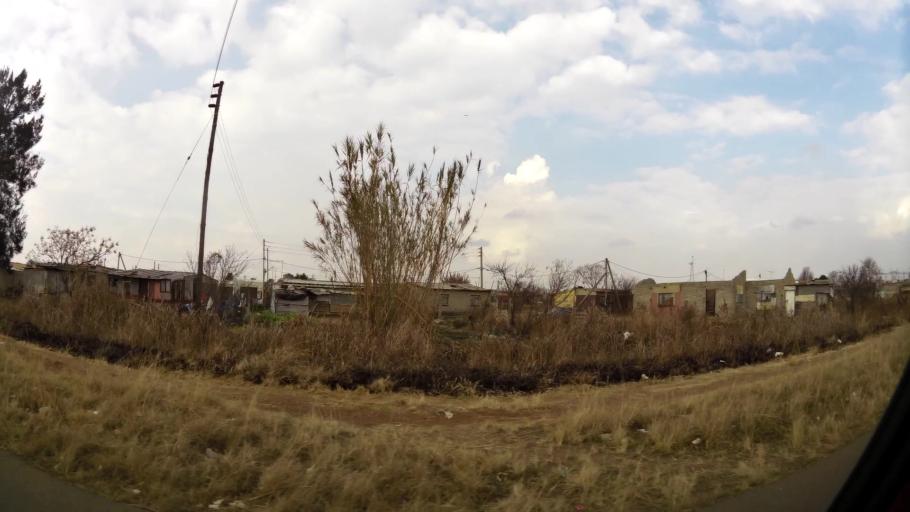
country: ZA
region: Gauteng
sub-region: Sedibeng District Municipality
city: Vanderbijlpark
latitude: -26.6736
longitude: 27.8597
